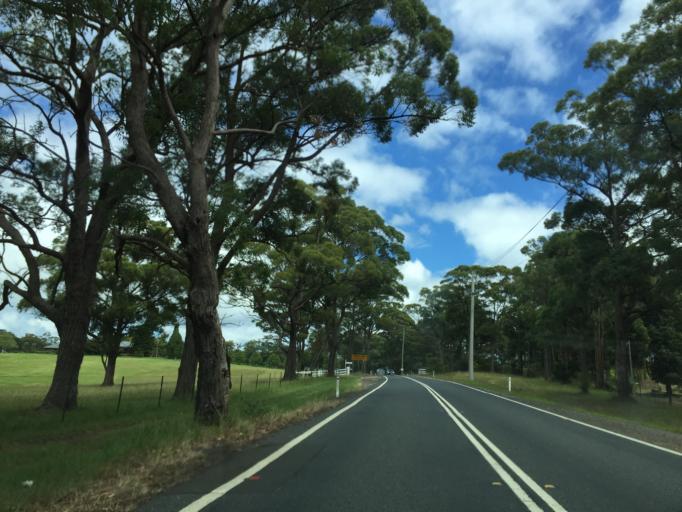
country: AU
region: New South Wales
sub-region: Hawkesbury
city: Richmond
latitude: -33.5153
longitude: 150.6077
